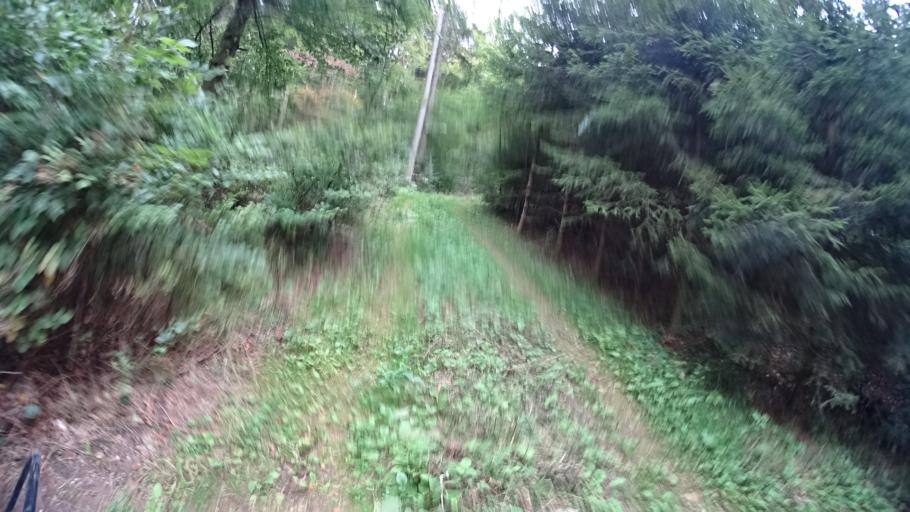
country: DE
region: Bavaria
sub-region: Upper Bavaria
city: Hitzhofen
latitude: 48.8868
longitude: 11.3276
